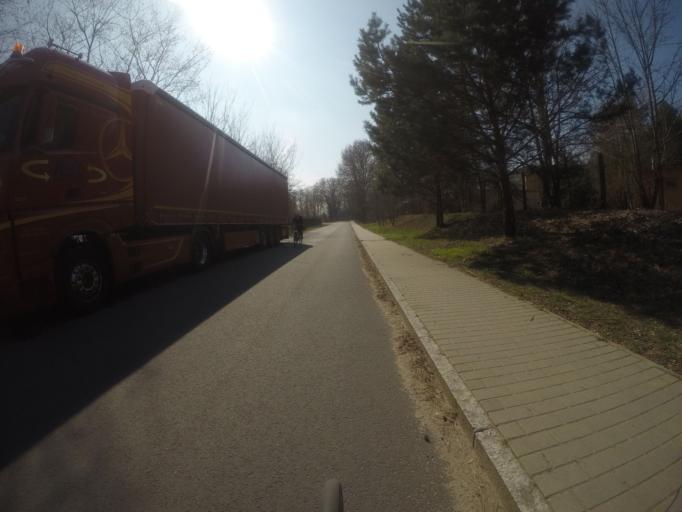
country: DE
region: Berlin
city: Muggelheim
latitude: 52.3873
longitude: 13.7023
